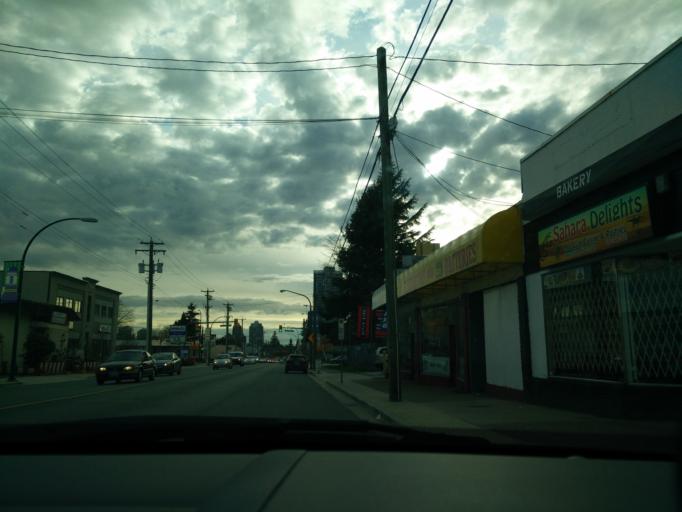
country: CA
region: British Columbia
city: New Westminster
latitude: 49.2215
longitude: -122.9458
